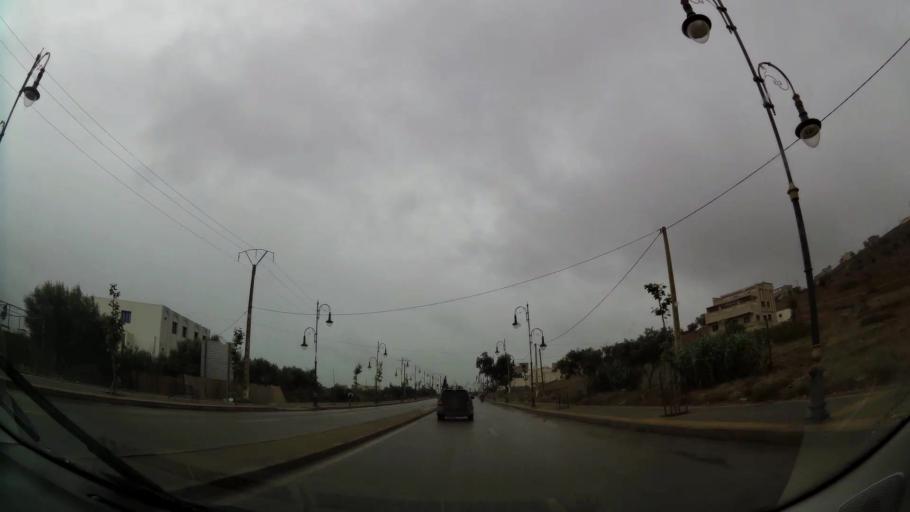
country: MA
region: Taza-Al Hoceima-Taounate
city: Imzourene
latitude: 35.1702
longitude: -3.8605
